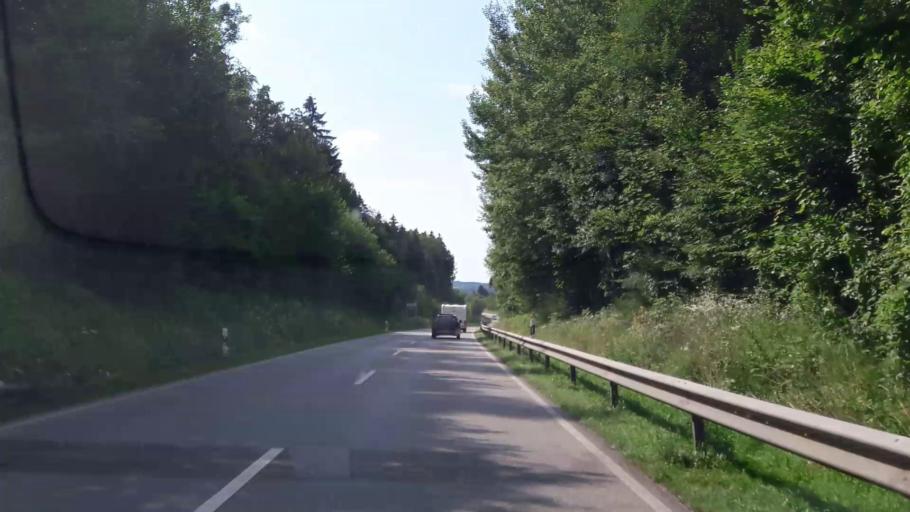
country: DE
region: Bavaria
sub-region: Upper Bavaria
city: Teisendorf
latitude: 47.8396
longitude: 12.8270
